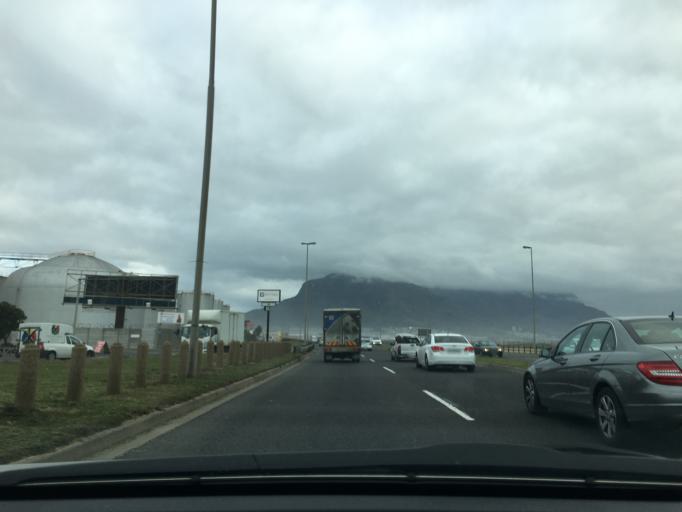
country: ZA
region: Western Cape
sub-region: City of Cape Town
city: Sunset Beach
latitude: -33.9007
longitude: 18.4781
